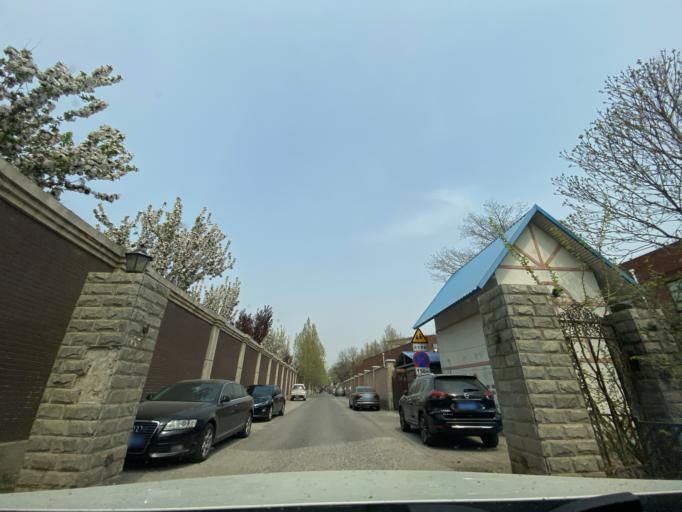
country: CN
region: Beijing
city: Sijiqing
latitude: 39.9406
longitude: 116.2457
